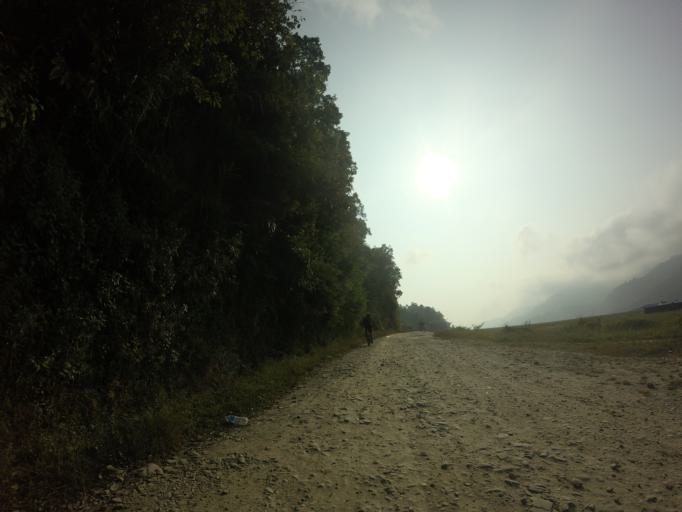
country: NP
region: Western Region
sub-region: Gandaki Zone
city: Pokhara
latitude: 28.2348
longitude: 83.9141
